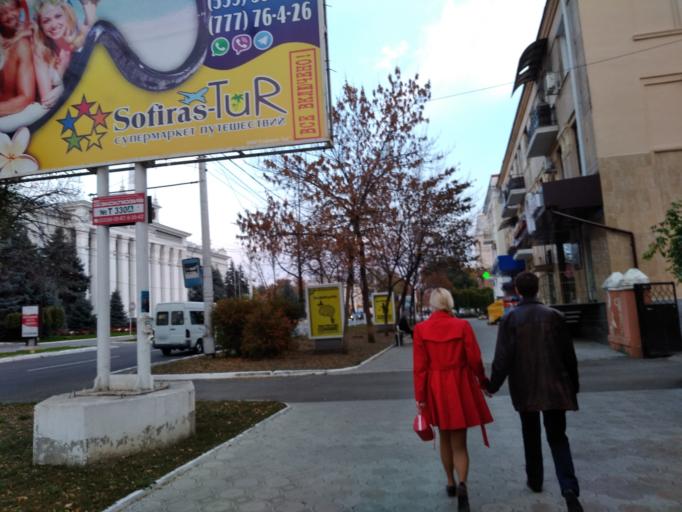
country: MD
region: Telenesti
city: Tiraspolul Nou
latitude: 46.8366
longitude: 29.6271
